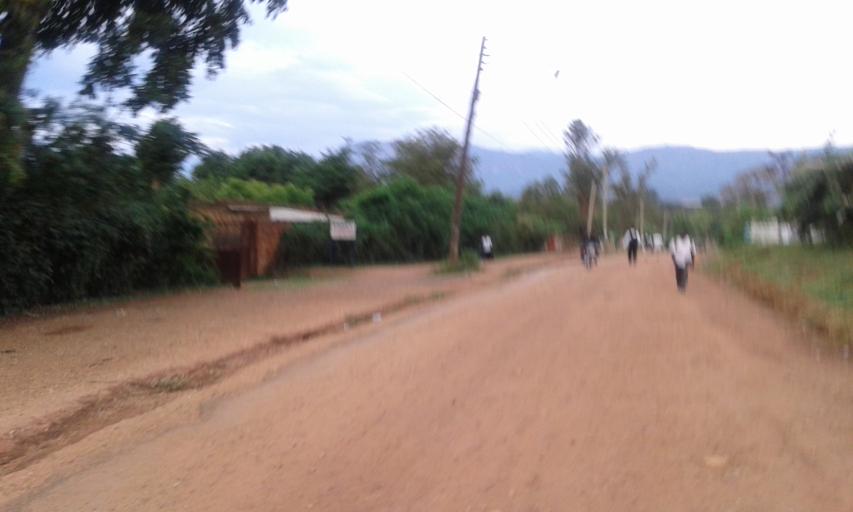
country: UG
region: Eastern Region
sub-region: Mbale District
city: Mbale
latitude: 1.0810
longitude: 34.1722
